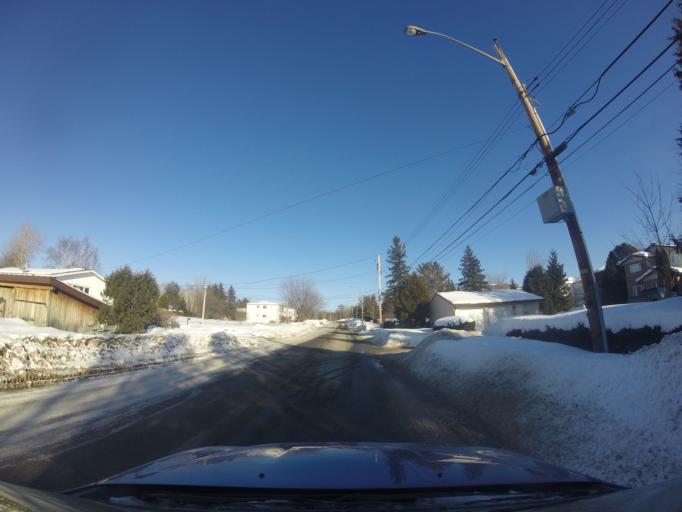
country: CA
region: Ontario
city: Greater Sudbury
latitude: 46.4616
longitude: -80.9992
